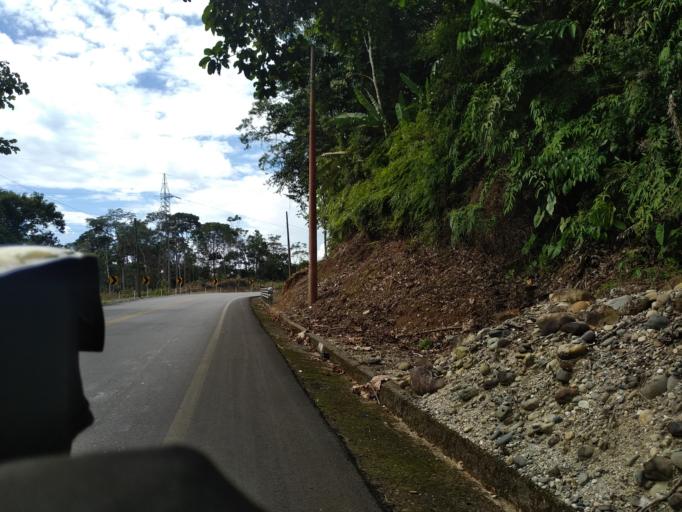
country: EC
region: Napo
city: Tena
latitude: -1.1146
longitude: -77.8081
